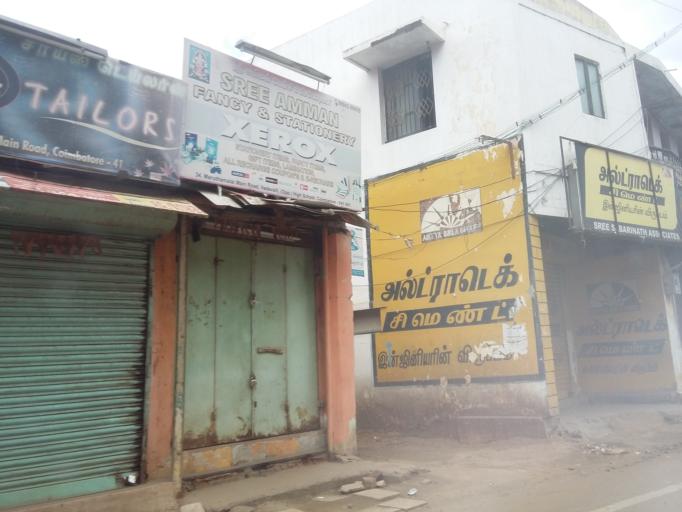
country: IN
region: Tamil Nadu
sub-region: Coimbatore
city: Perur
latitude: 11.0239
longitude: 76.9085
